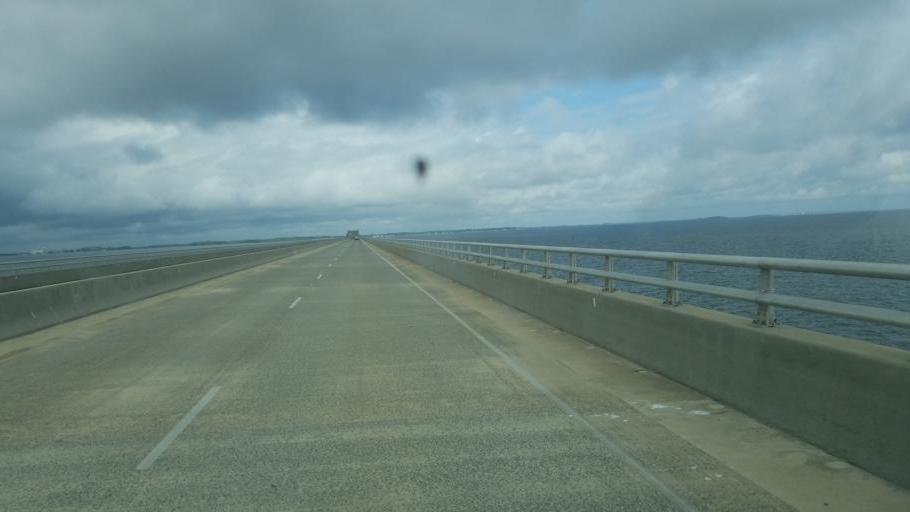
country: US
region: North Carolina
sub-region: Dare County
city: Manteo
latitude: 35.8835
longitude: -75.6984
